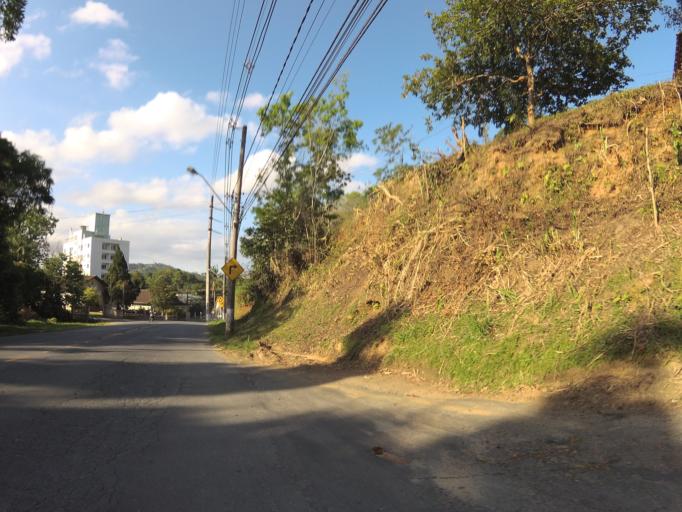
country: BR
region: Santa Catarina
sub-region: Blumenau
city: Blumenau
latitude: -26.9249
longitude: -49.1084
